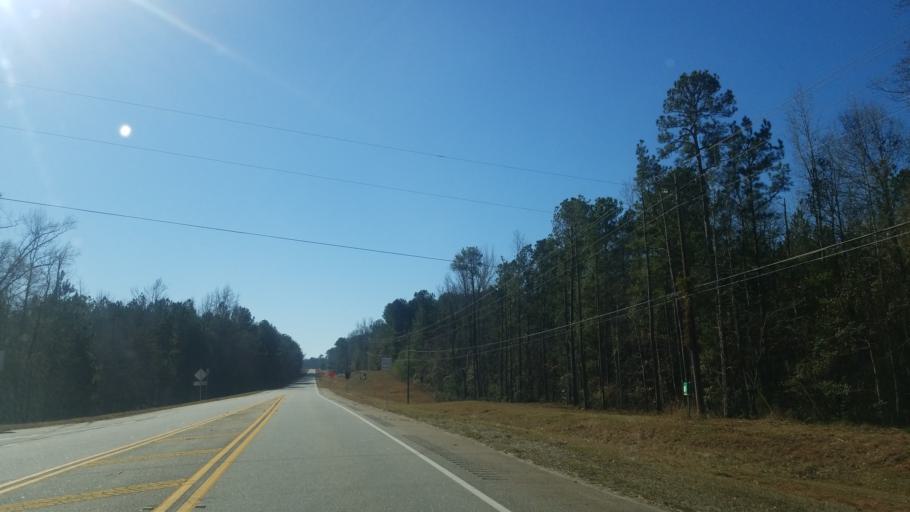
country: US
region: Alabama
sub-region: Lee County
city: Smiths Station
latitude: 32.6726
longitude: -85.0587
